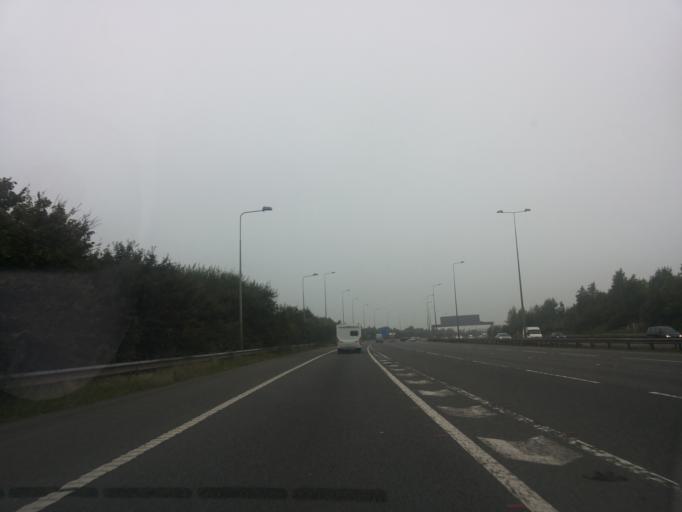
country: GB
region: England
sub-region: Borough of Tameside
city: Droylsden
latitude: 53.4622
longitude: -2.1386
